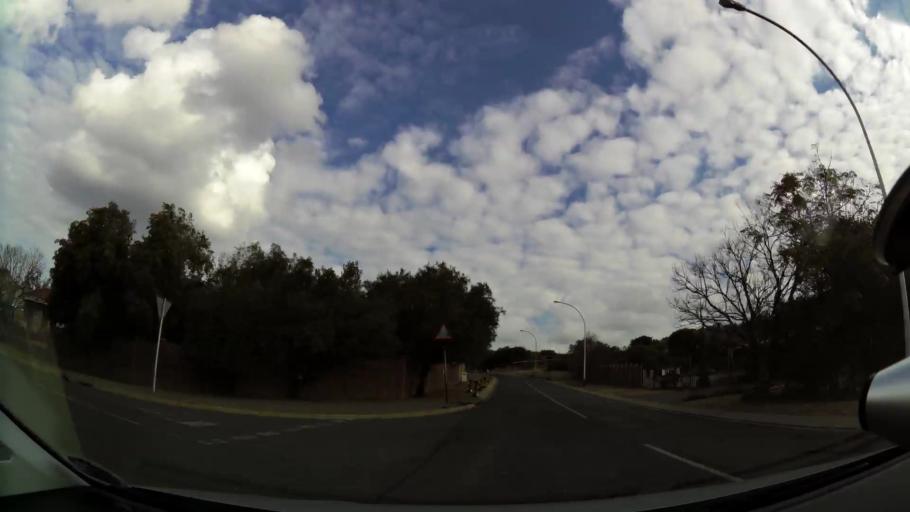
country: ZA
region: Orange Free State
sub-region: Mangaung Metropolitan Municipality
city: Bloemfontein
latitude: -29.0734
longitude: 26.2085
